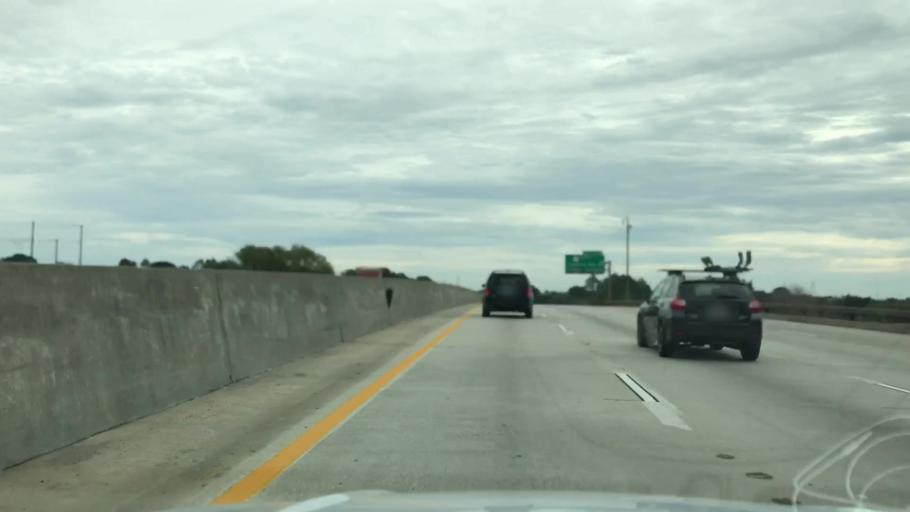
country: US
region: South Carolina
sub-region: Charleston County
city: North Charleston
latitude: 32.8438
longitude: -79.9812
